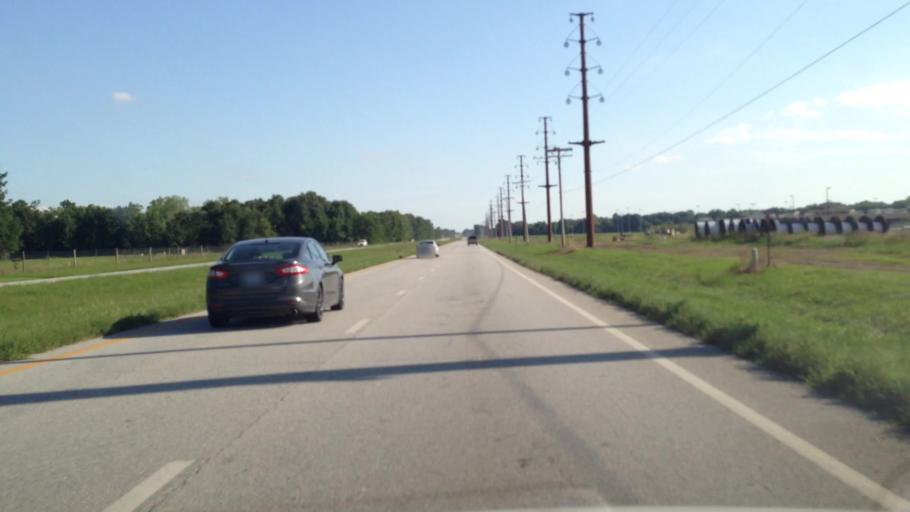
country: US
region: Kansas
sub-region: Crawford County
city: Frontenac
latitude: 37.4836
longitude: -94.7053
